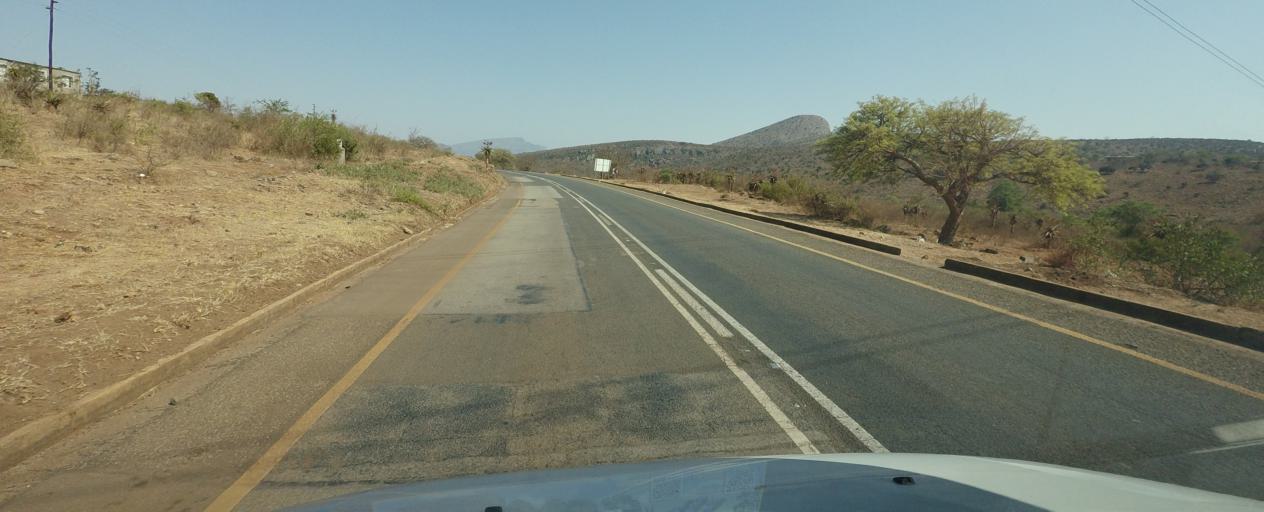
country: ZA
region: Limpopo
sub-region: Mopani District Municipality
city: Hoedspruit
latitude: -24.4702
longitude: 30.6298
